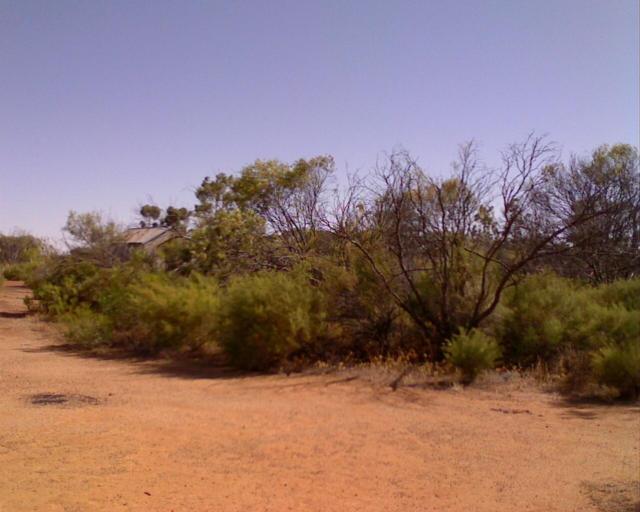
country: AU
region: Western Australia
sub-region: Moora
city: Moora
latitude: -29.8652
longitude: 116.1657
